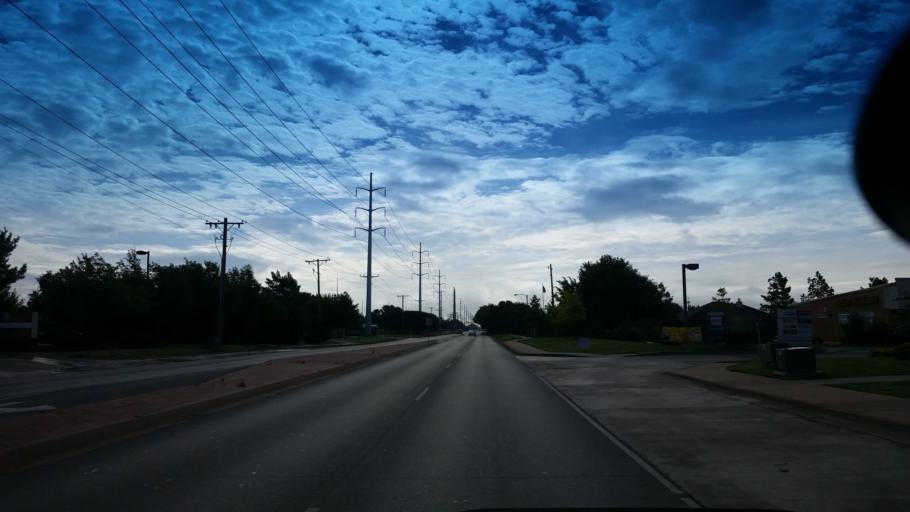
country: US
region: Oklahoma
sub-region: Oklahoma County
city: Edmond
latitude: 35.6675
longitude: -97.5108
